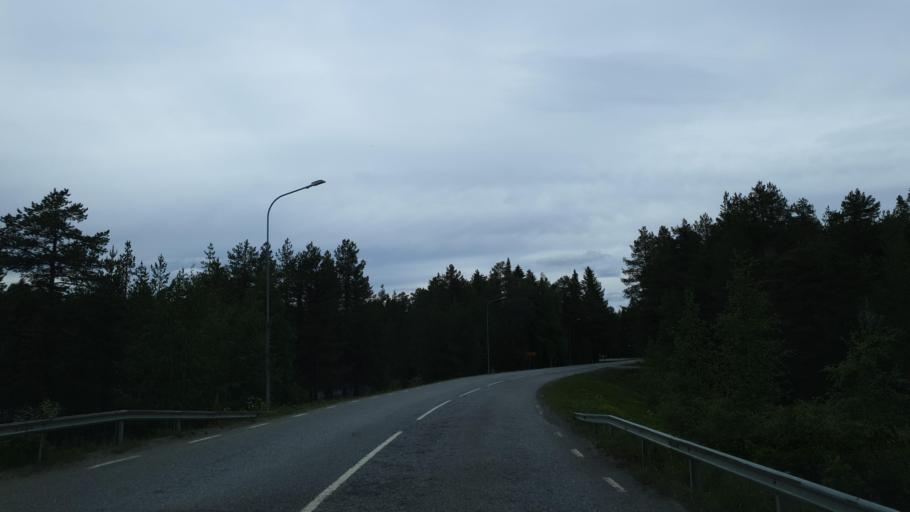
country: SE
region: Vaesterbotten
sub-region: Sorsele Kommun
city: Sorsele
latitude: 65.5445
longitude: 17.5083
